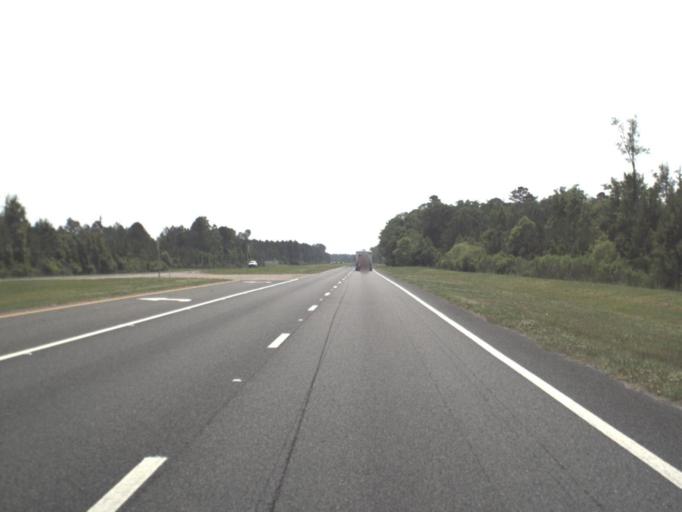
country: US
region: Florida
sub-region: Nassau County
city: Yulee
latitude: 30.6143
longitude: -81.6953
